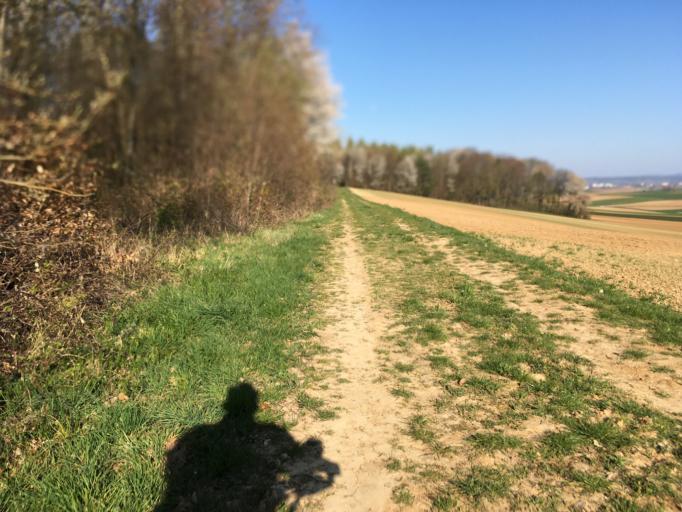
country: DE
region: Baden-Wuerttemberg
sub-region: Regierungsbezirk Stuttgart
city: Leingarten
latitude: 49.1646
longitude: 9.1030
